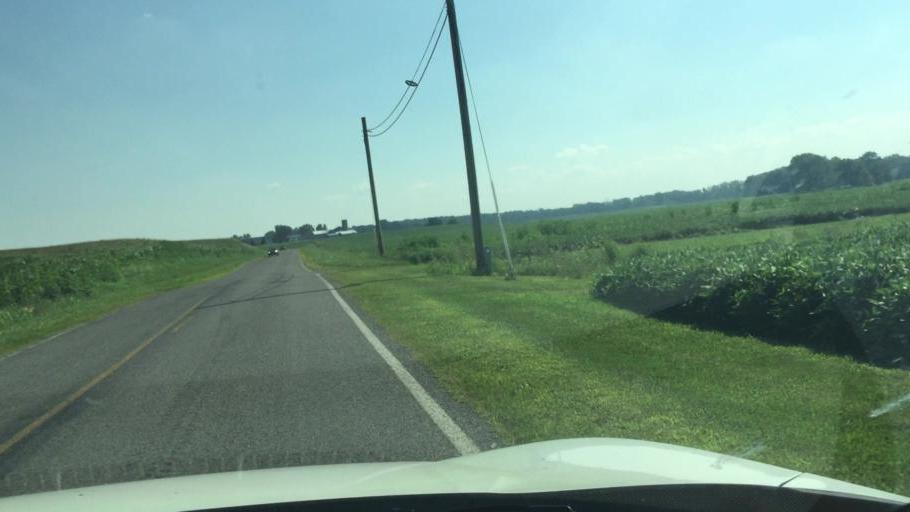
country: US
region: Ohio
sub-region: Champaign County
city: Mechanicsburg
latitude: 40.0646
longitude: -83.6511
